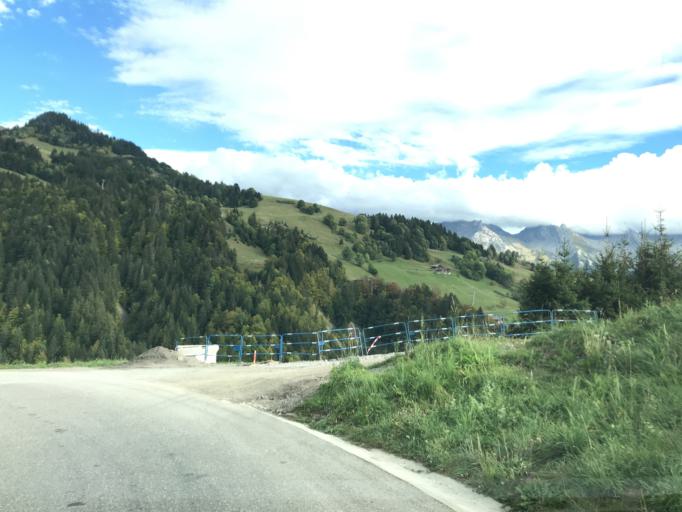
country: FR
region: Rhone-Alpes
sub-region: Departement de la Haute-Savoie
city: Le Grand-Bornand
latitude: 45.9553
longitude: 6.4373
